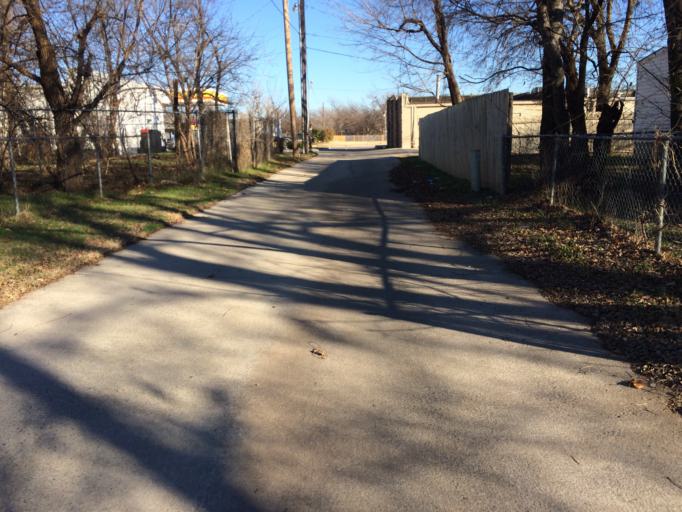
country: US
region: Oklahoma
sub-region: Cleveland County
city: Norman
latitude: 35.2272
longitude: -97.4420
